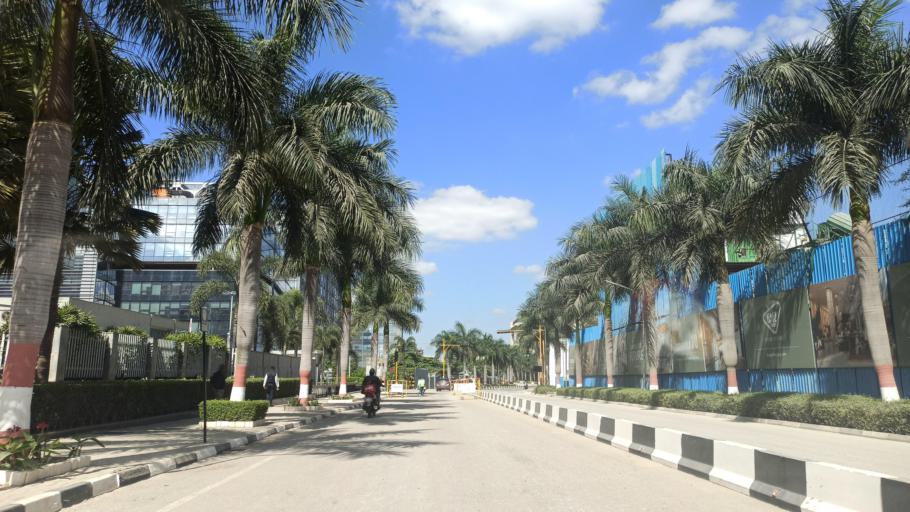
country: IN
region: Karnataka
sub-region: Bangalore Urban
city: Bangalore
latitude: 12.9215
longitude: 77.6855
